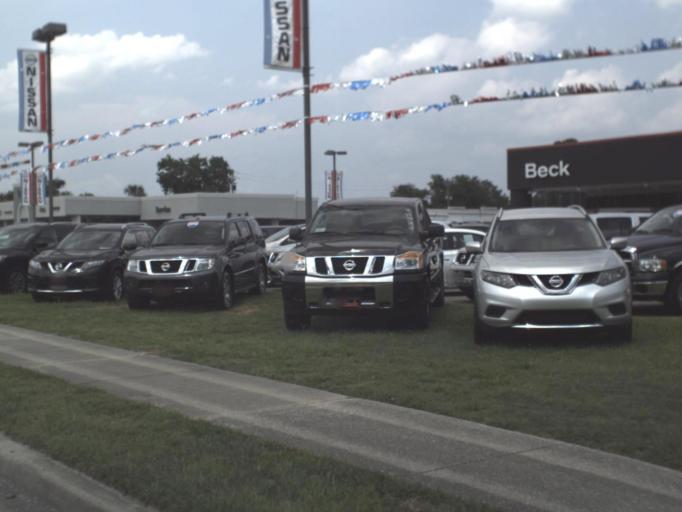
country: US
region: Florida
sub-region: Putnam County
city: Palatka
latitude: 29.6629
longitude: -81.6561
